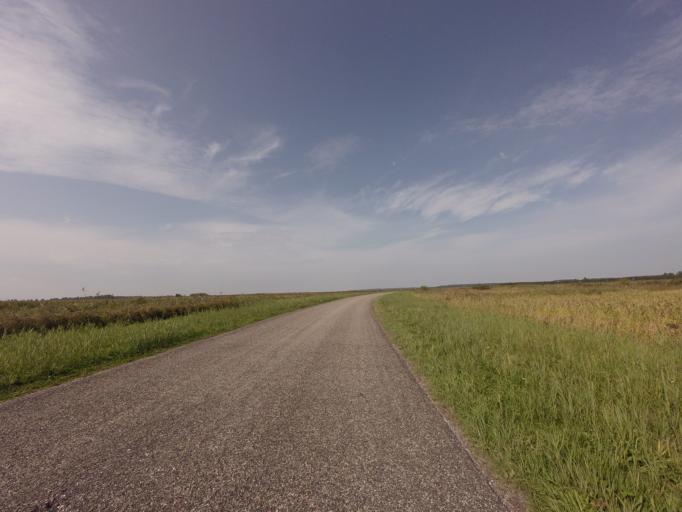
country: NL
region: Groningen
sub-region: Gemeente De Marne
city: Ulrum
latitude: 53.3476
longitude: 6.2686
